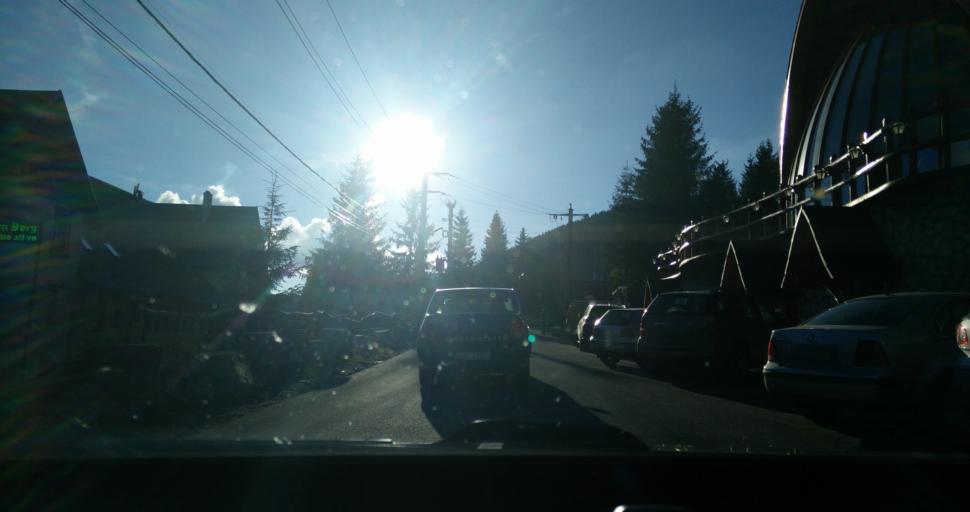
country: RO
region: Alba
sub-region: Comuna Arieseni
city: Arieseni
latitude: 46.5159
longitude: 22.6682
